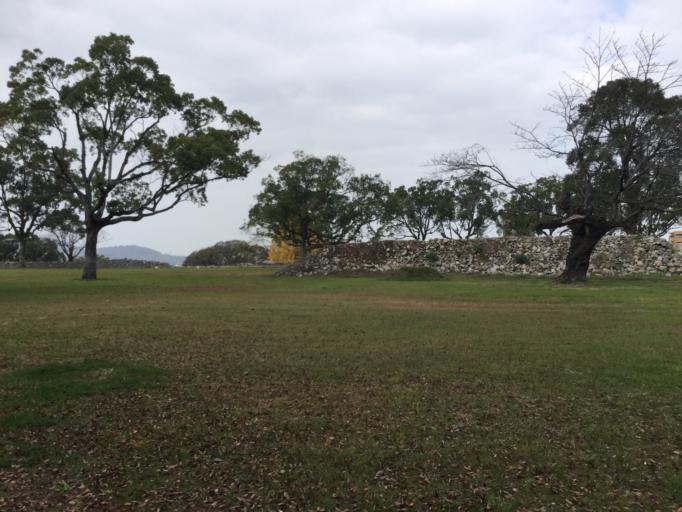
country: JP
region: Kumamoto
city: Kumamoto
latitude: 32.8081
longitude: 130.7028
